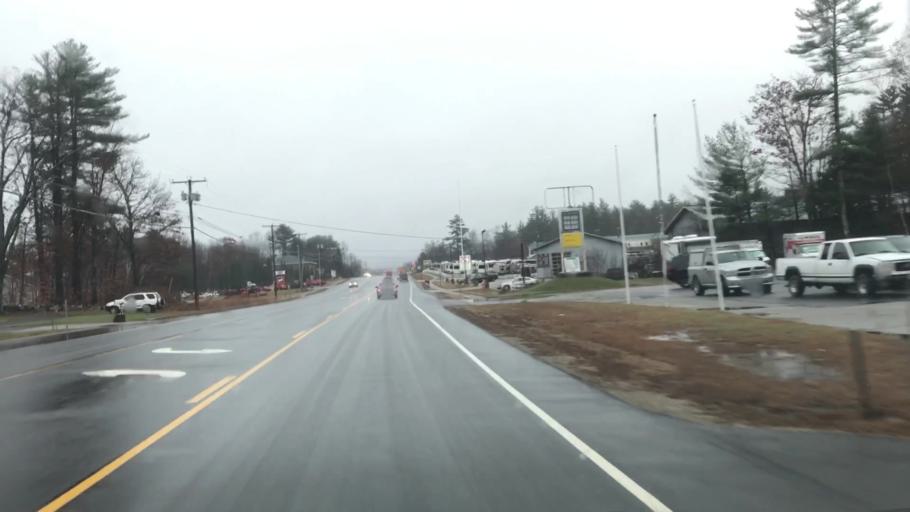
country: US
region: New Hampshire
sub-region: Merrimack County
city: Chichester
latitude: 43.2468
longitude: -71.4108
